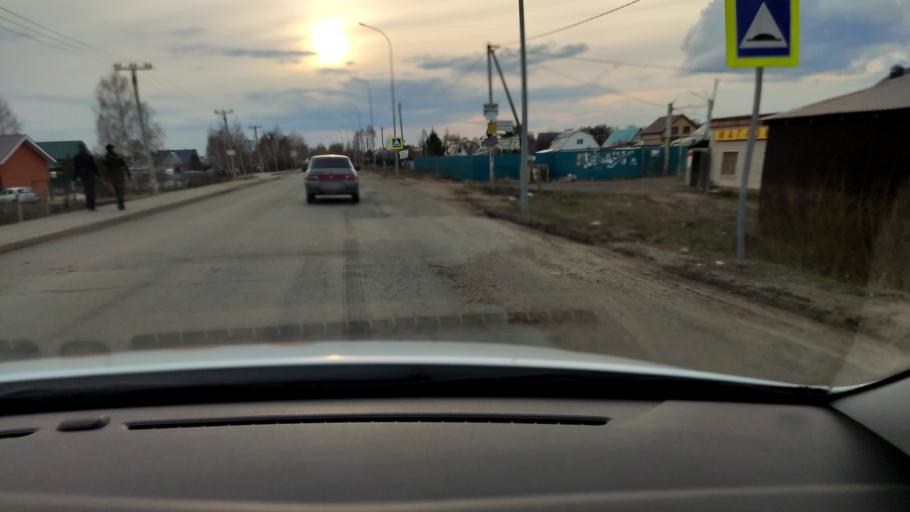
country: RU
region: Tatarstan
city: Stolbishchi
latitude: 55.6938
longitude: 49.2117
